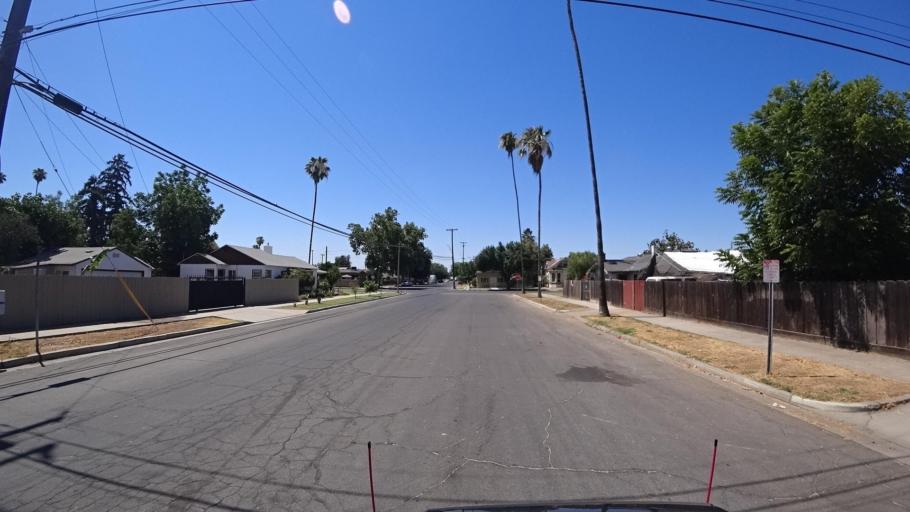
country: US
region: California
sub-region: Fresno County
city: Fresno
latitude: 36.7387
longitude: -119.7563
